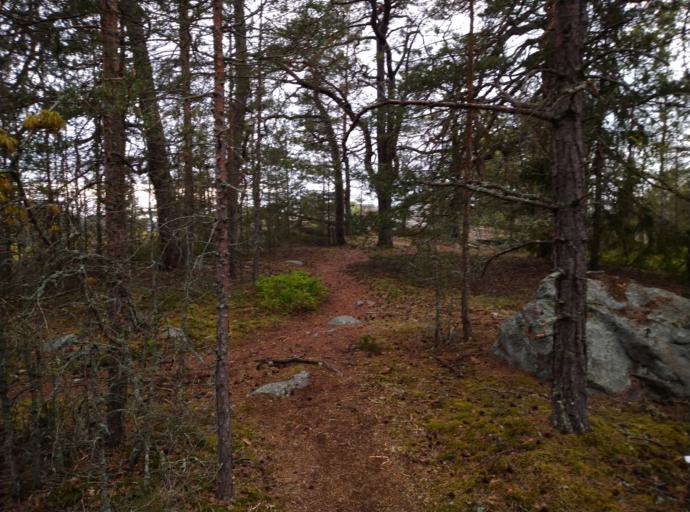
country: SE
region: Stockholm
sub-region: Nacka Kommun
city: Fisksatra
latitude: 59.2972
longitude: 18.2805
